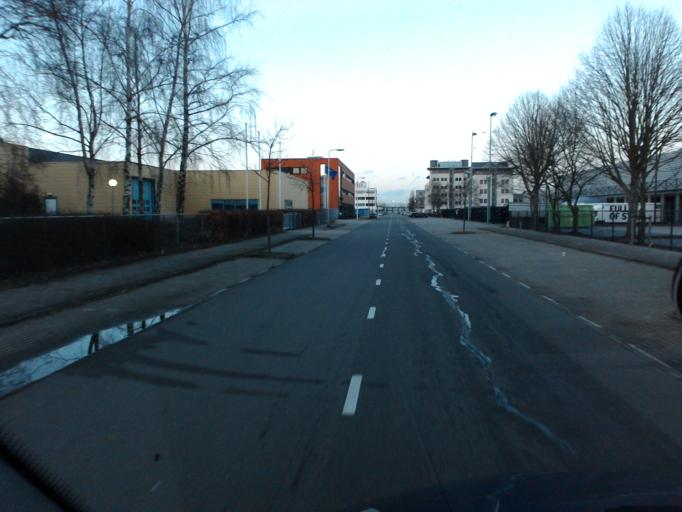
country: NL
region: Utrecht
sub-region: Stichtse Vecht
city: Maarssen
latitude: 52.1128
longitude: 5.0484
